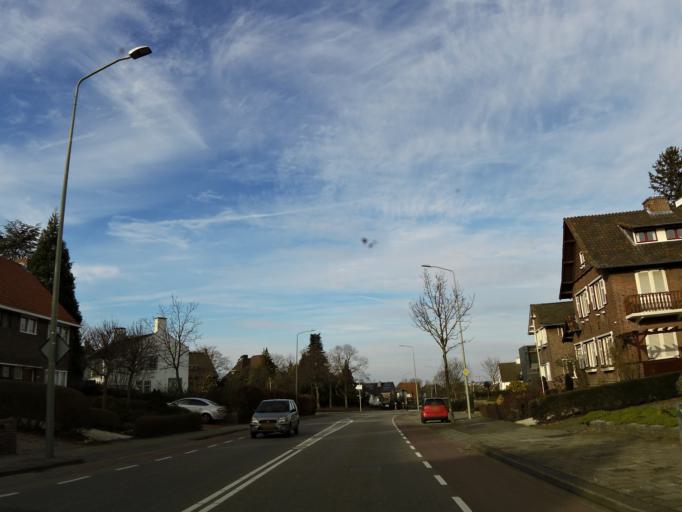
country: NL
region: Limburg
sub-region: Gemeente Heerlen
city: Heerlen
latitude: 50.8754
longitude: 5.9898
